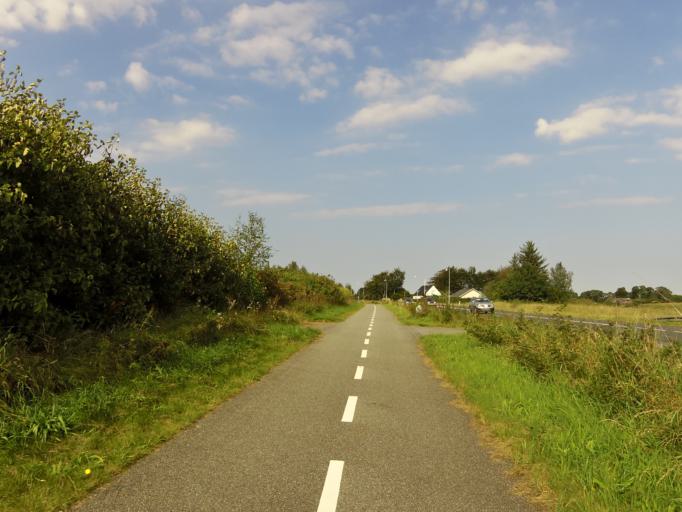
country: DK
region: South Denmark
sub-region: Vejen Kommune
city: Vejen
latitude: 55.4466
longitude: 9.1375
